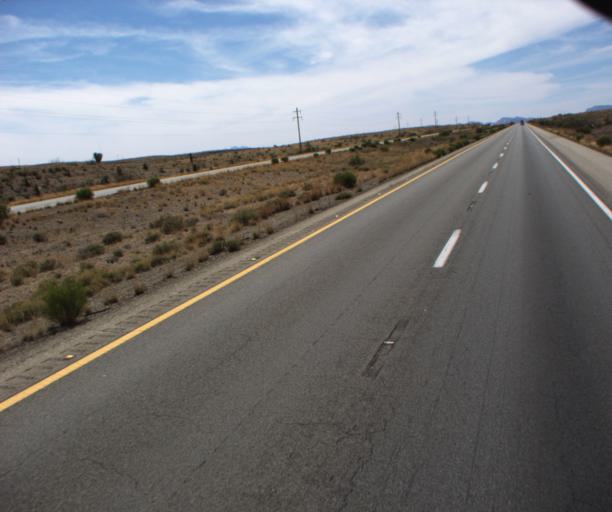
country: US
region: Arizona
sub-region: Cochise County
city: Willcox
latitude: 32.3511
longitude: -109.7303
